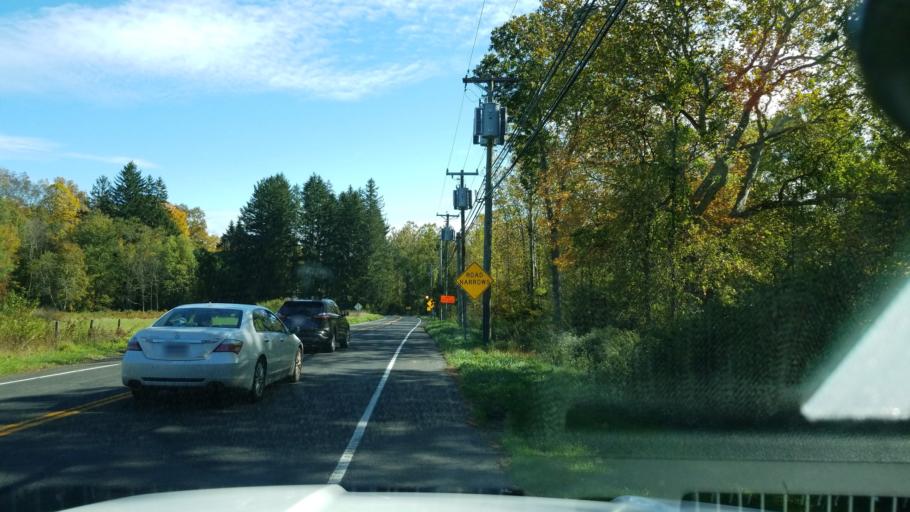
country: US
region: Connecticut
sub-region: Litchfield County
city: New Milford
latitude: 41.5494
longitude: -73.3387
